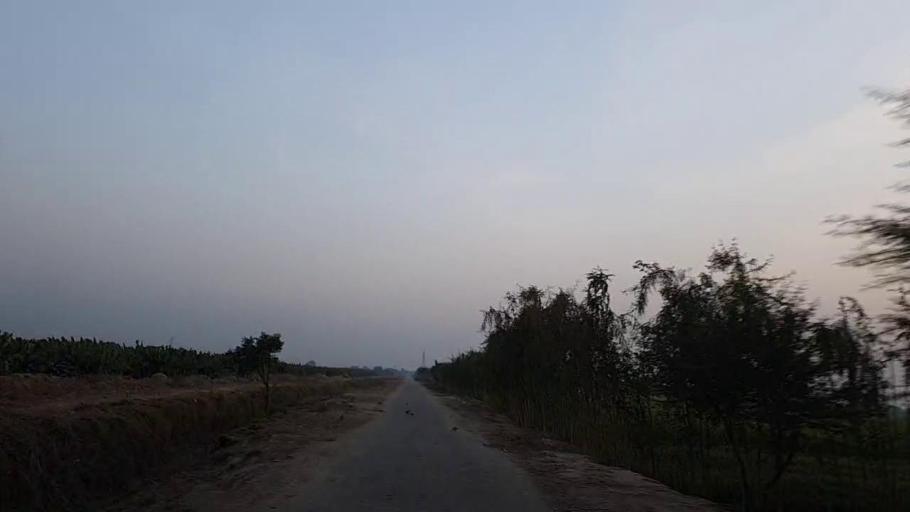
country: PK
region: Sindh
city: Tando Ghulam Ali
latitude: 25.1151
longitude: 68.8988
